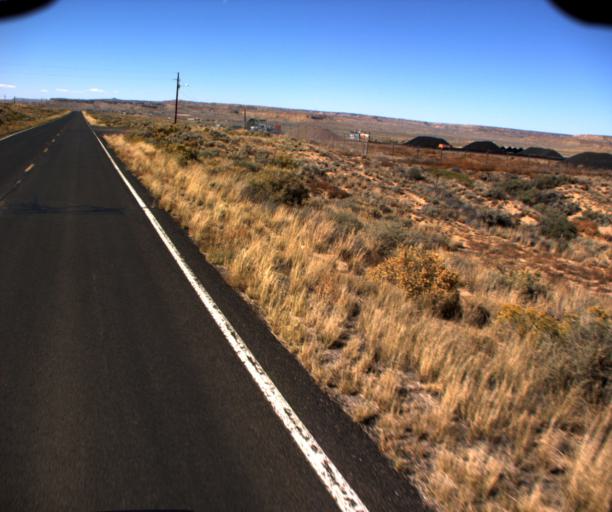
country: US
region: Arizona
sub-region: Navajo County
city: First Mesa
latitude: 35.8729
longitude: -110.5625
